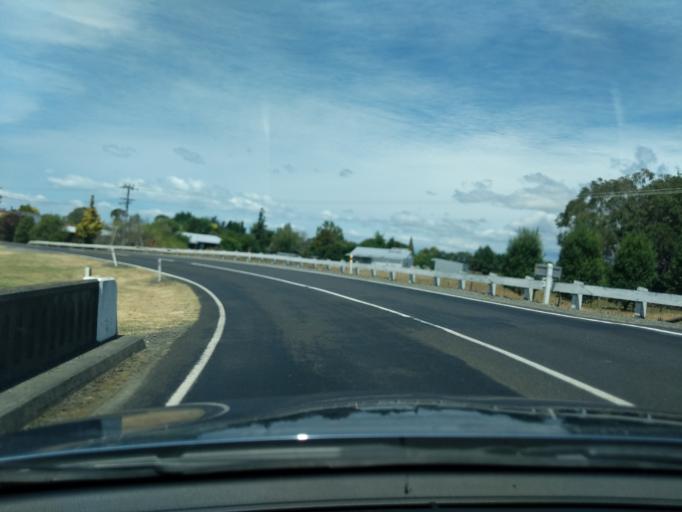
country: NZ
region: Tasman
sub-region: Tasman District
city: Motueka
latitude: -41.0756
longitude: 172.9953
